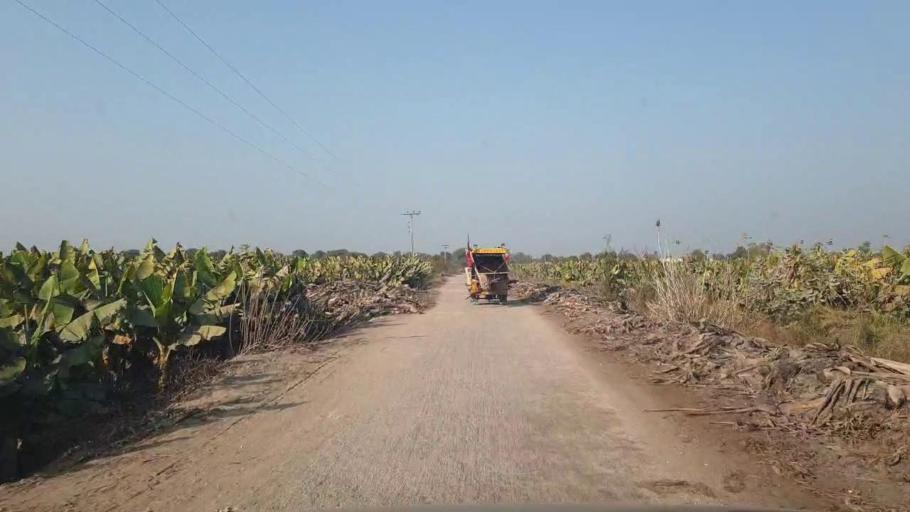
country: PK
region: Sindh
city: Bhit Shah
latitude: 25.8209
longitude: 68.5139
